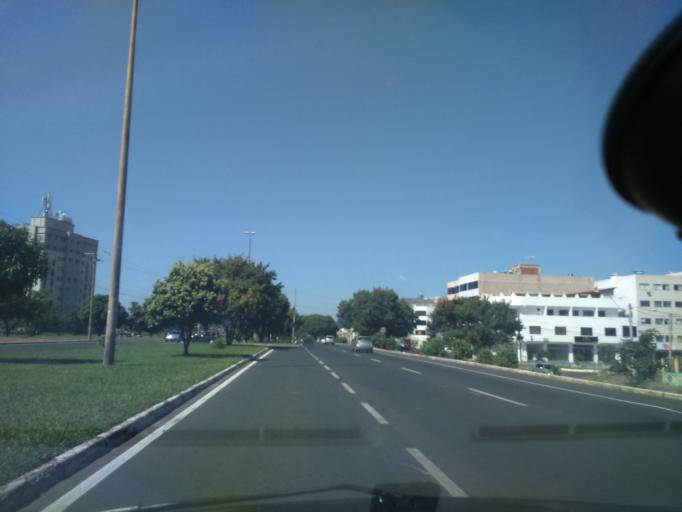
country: BR
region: Federal District
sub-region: Brasilia
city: Brasilia
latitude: -15.8483
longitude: -47.9752
